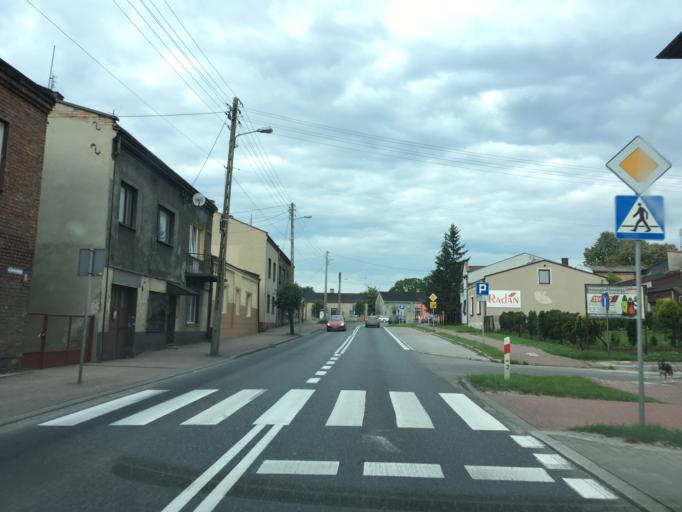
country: PL
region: Silesian Voivodeship
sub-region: Powiat zawiercianski
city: Szczekociny
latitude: 50.6264
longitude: 19.8201
